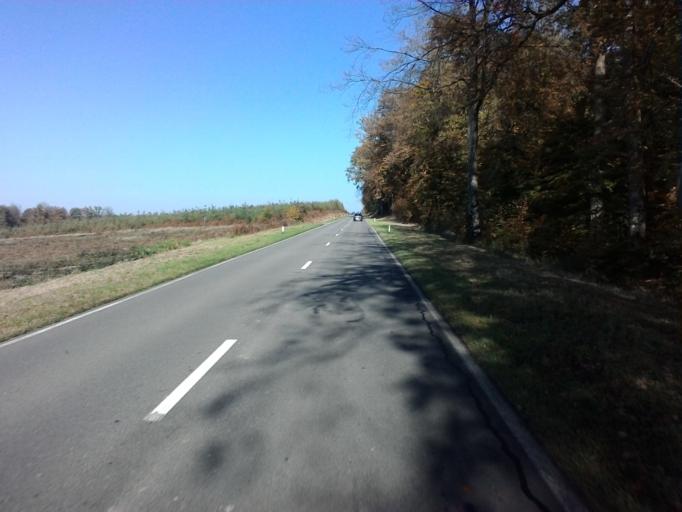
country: BE
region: Wallonia
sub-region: Province du Luxembourg
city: Chiny
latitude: 49.7644
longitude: 5.3207
